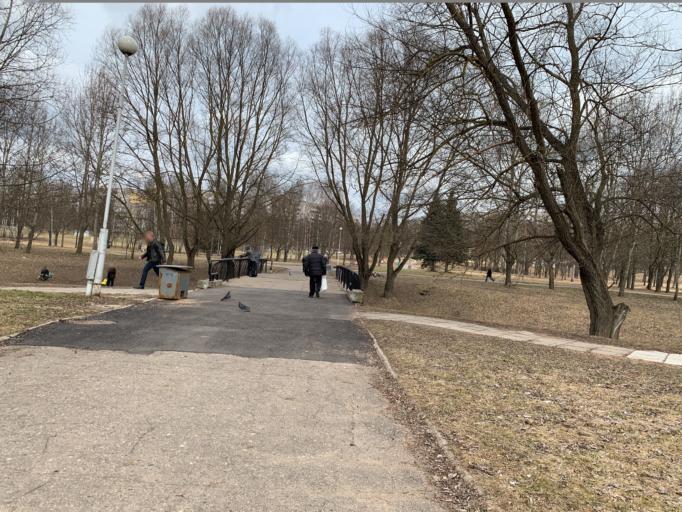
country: BY
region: Minsk
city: Borovlyany
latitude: 53.9511
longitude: 27.6301
